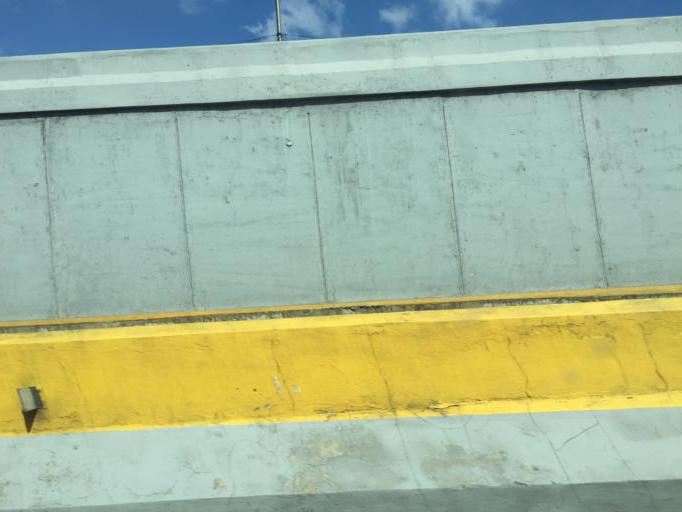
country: DO
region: Santo Domingo
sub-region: Santo Domingo
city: Santo Domingo Este
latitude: 18.4849
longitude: -69.8652
